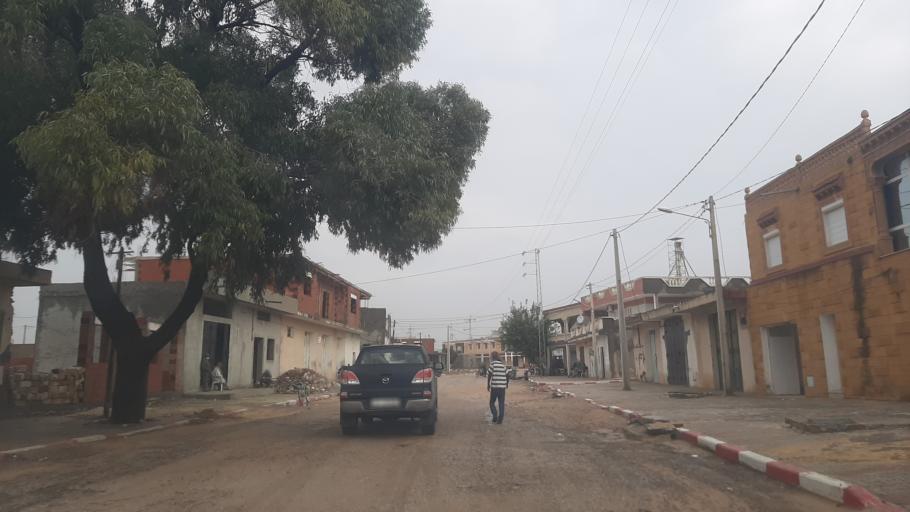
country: TN
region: Al Munastir
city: Sidi Bin Nur
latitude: 35.4802
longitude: 10.8732
